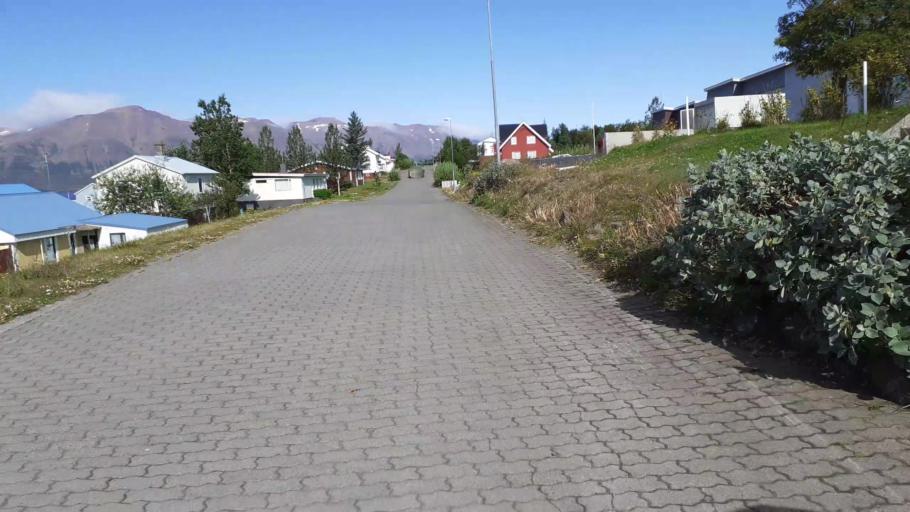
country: IS
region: Northeast
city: Dalvik
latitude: 65.9799
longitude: -18.3759
